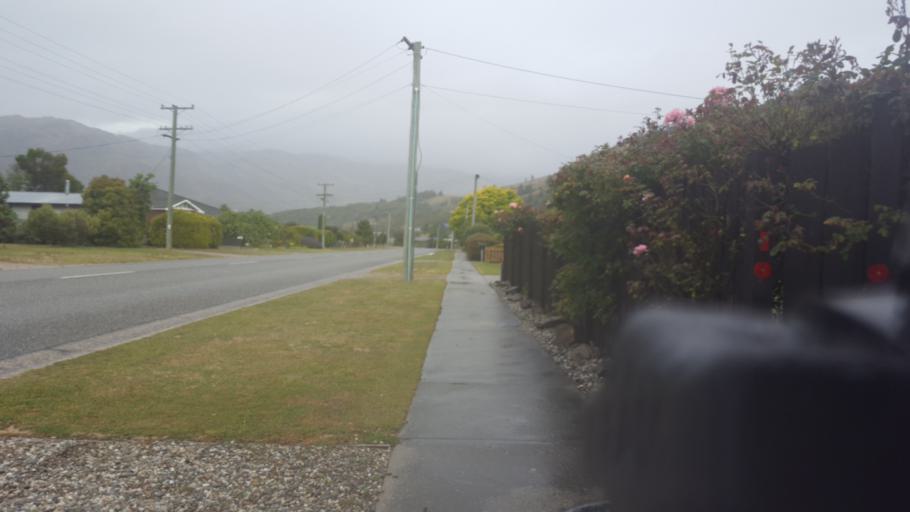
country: NZ
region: Otago
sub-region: Queenstown-Lakes District
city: Wanaka
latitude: -45.1893
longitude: 169.3261
